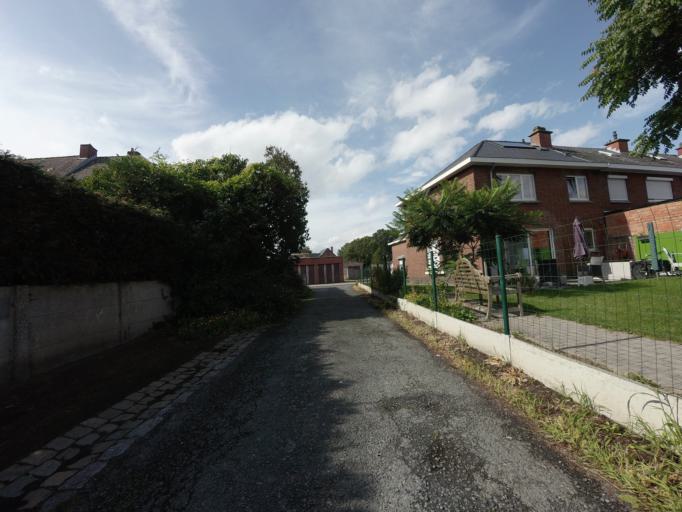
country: BE
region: Flanders
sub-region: Provincie Vlaams-Brabant
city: Kapelle-op-den-Bos
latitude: 51.0327
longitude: 4.3617
